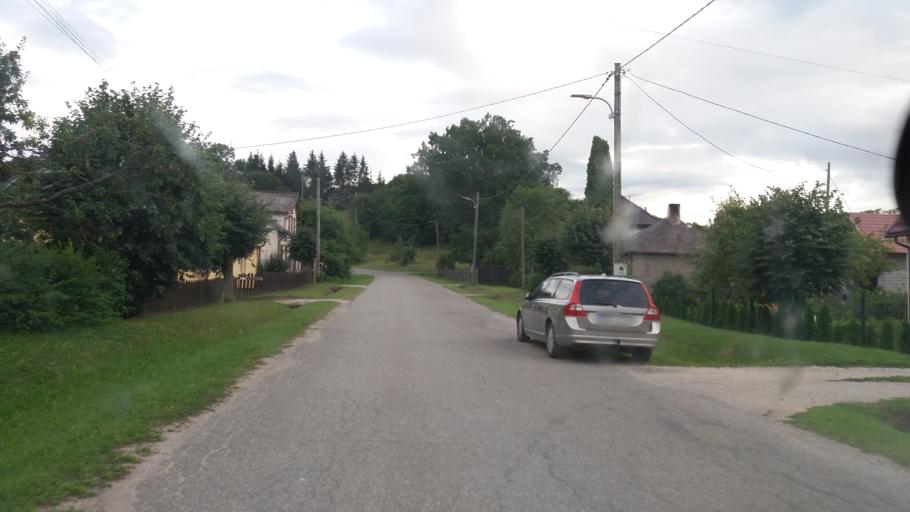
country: LV
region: Talsu Rajons
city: Sabile
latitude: 57.0418
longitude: 22.5688
